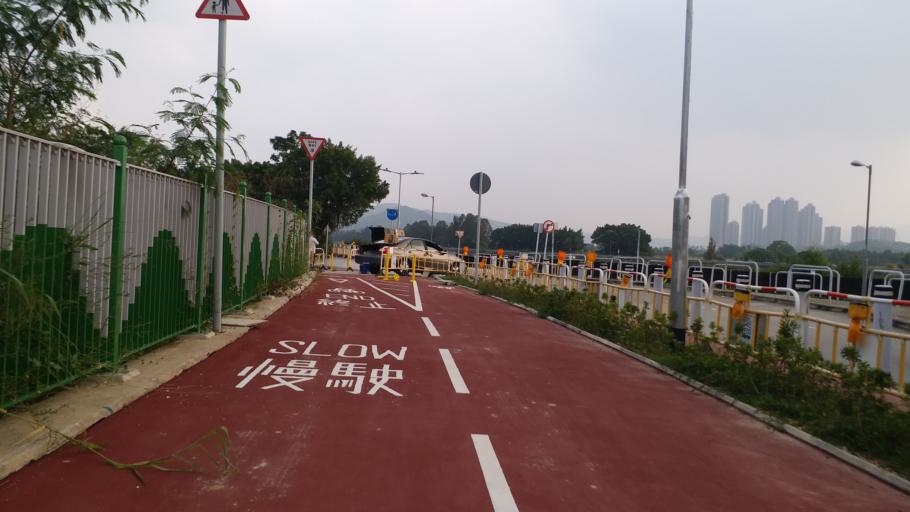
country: HK
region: Yuen Long
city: Yuen Long Kau Hui
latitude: 22.4642
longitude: 114.0448
